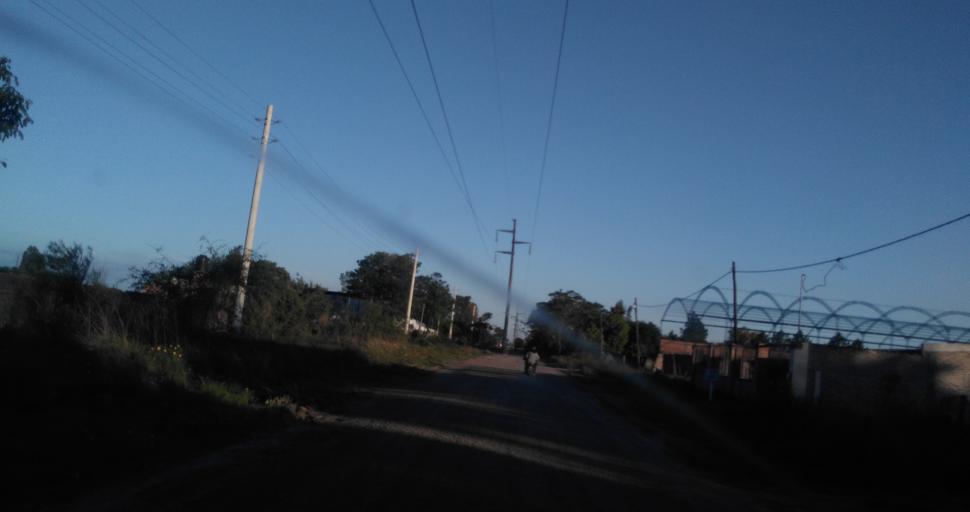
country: AR
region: Chaco
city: Fontana
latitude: -27.3995
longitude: -59.0019
